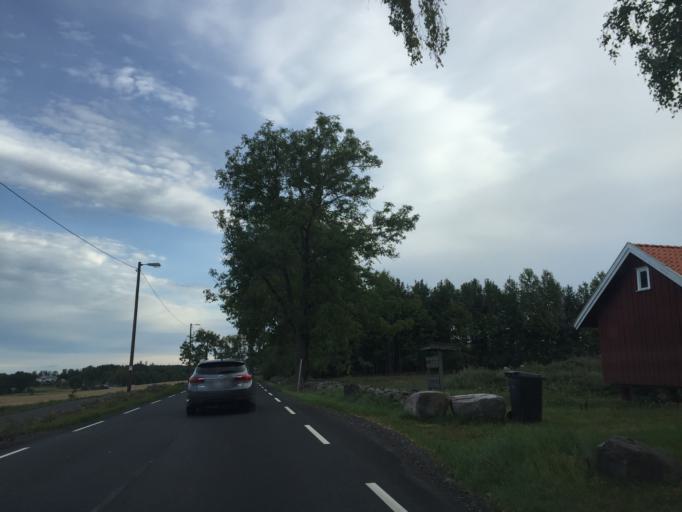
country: NO
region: Akershus
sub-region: As
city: As
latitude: 59.7117
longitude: 10.7728
